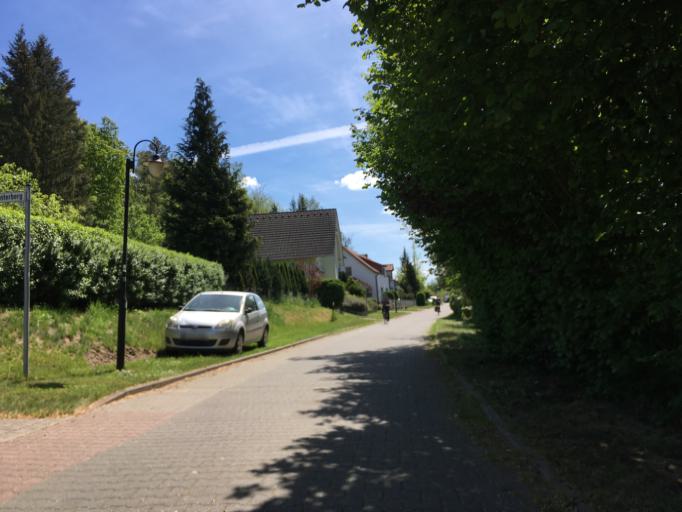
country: DE
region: Brandenburg
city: Niederfinow
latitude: 52.8436
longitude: 13.8980
